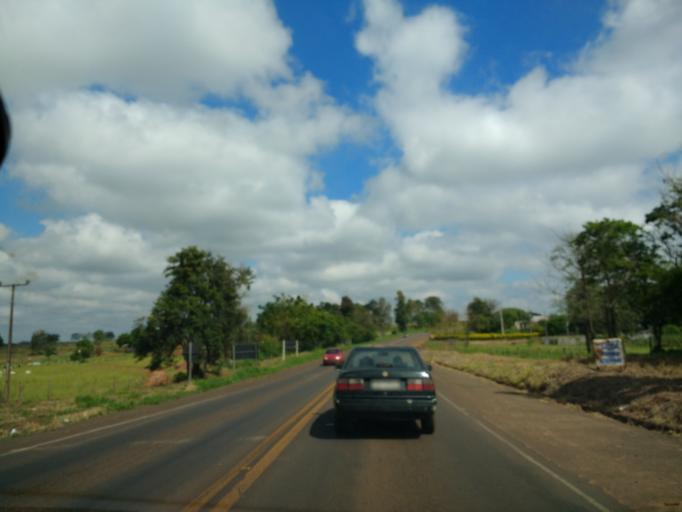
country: BR
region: Parana
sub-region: Cruzeiro Do Oeste
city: Cruzeiro do Oeste
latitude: -23.7964
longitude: -53.0490
